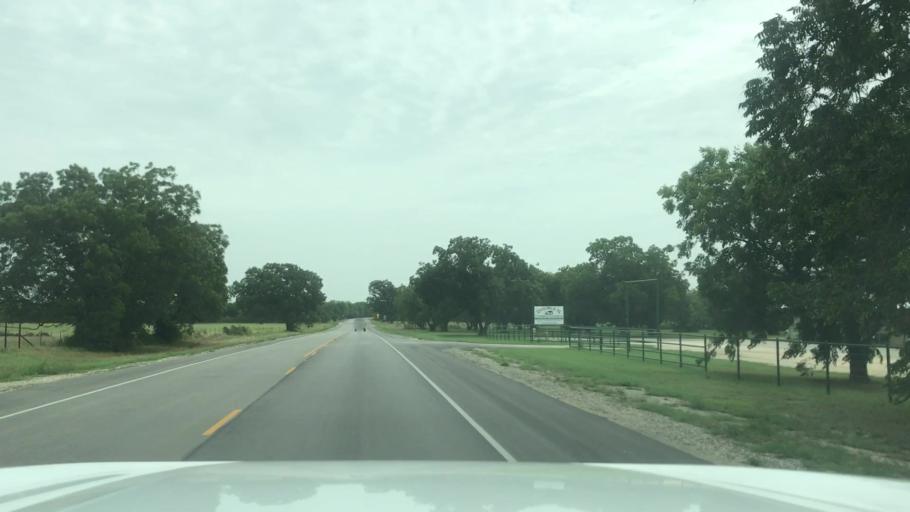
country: US
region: Texas
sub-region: Erath County
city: Dublin
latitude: 32.0911
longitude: -98.2765
